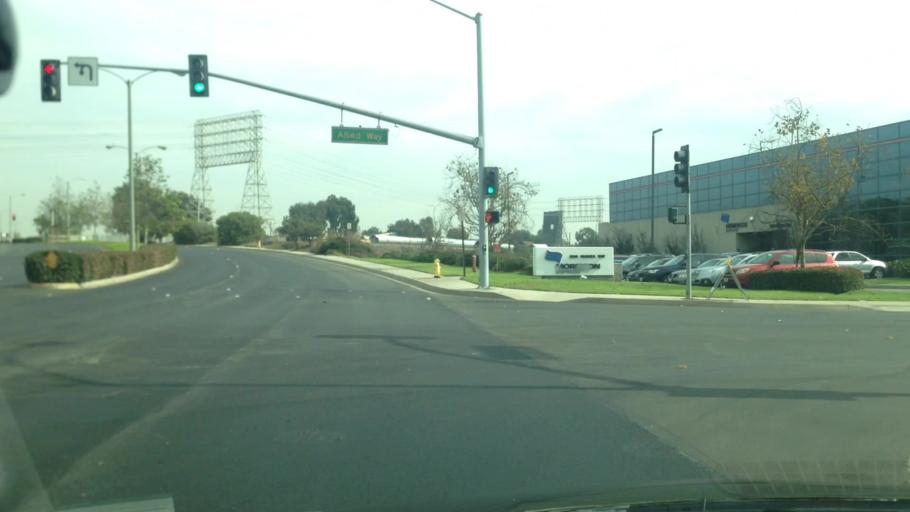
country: US
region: California
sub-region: Los Angeles County
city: Del Aire
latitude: 33.9084
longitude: -118.3920
